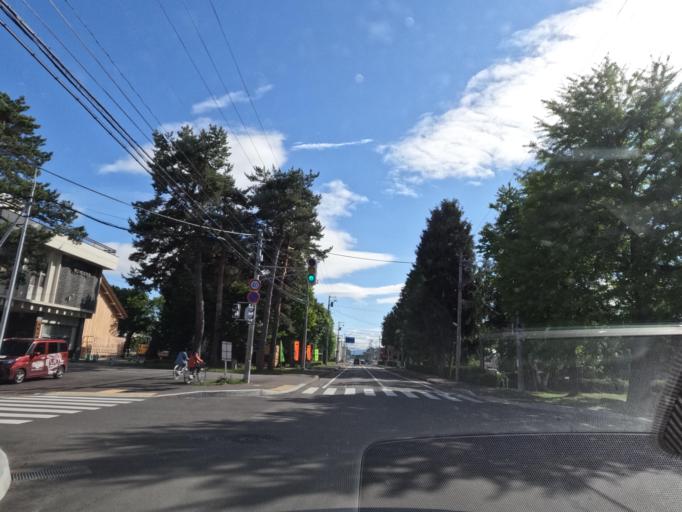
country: JP
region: Hokkaido
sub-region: Asahikawa-shi
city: Asahikawa
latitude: 43.6989
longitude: 142.5091
